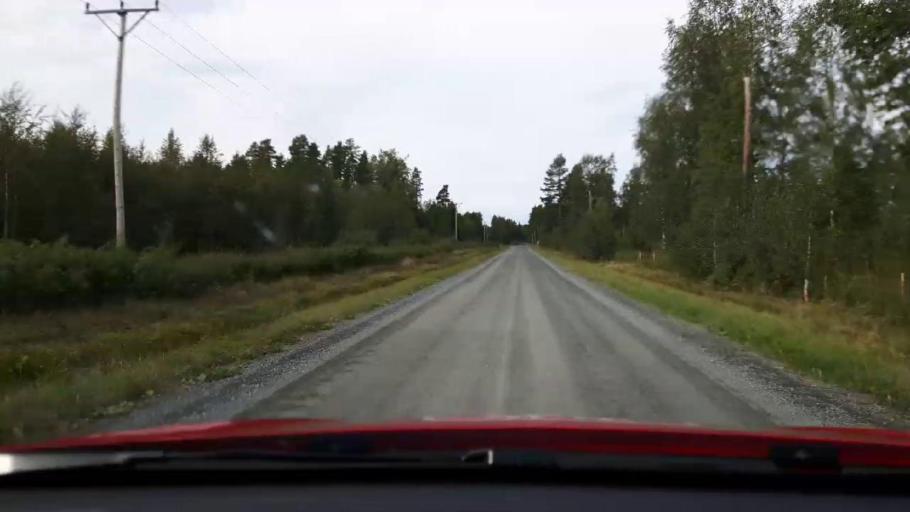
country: SE
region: Jaemtland
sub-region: Krokoms Kommun
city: Valla
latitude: 63.2574
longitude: 13.9369
